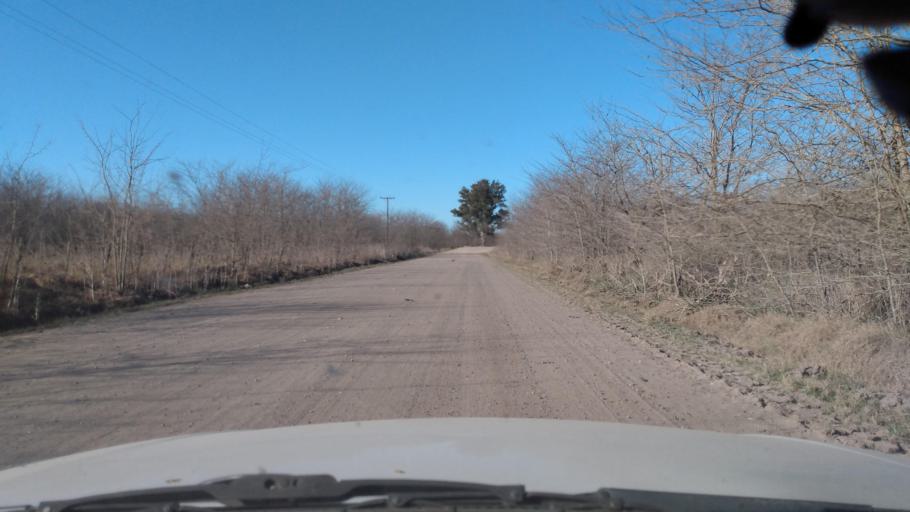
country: AR
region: Buenos Aires
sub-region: Partido de Mercedes
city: Mercedes
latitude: -34.6127
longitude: -59.3269
